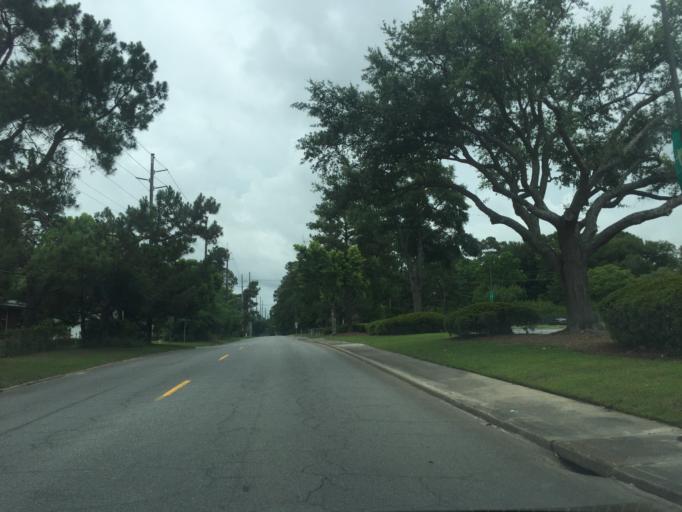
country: US
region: Georgia
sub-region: Chatham County
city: Thunderbolt
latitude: 32.0290
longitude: -81.1011
